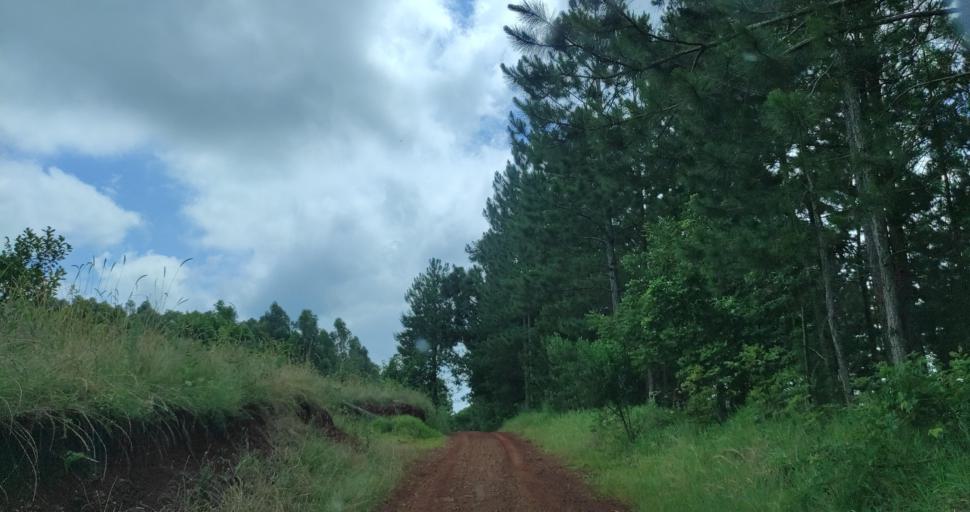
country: AR
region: Misiones
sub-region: Departamento de Veinticinco de Mayo
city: Veinticinco de Mayo
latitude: -27.4192
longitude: -54.7331
